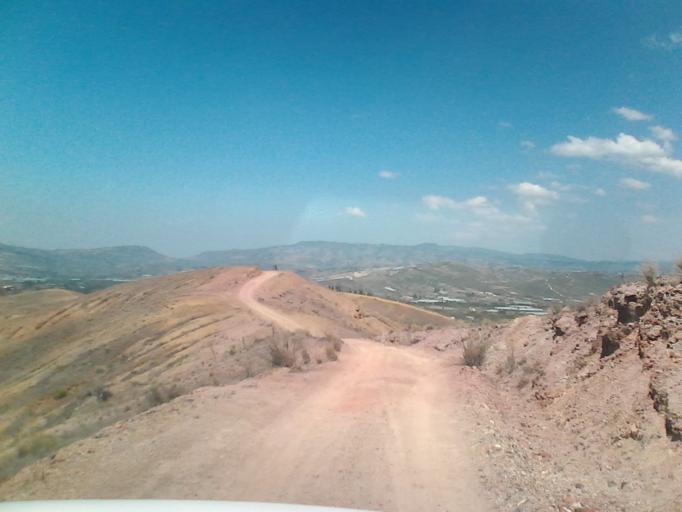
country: CO
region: Boyaca
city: Villa de Leiva
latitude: 5.6159
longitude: -73.5734
